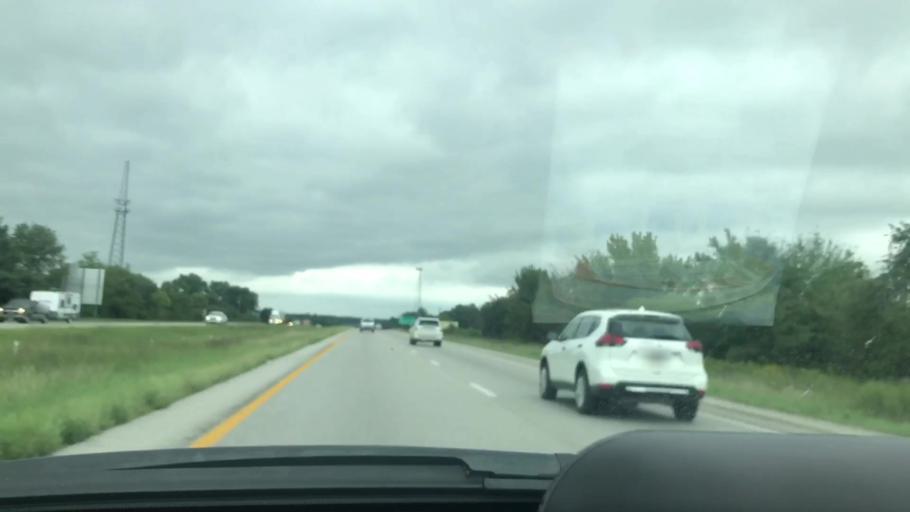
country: US
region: Missouri
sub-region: Jasper County
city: Duenweg
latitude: 37.0739
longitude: -94.3899
